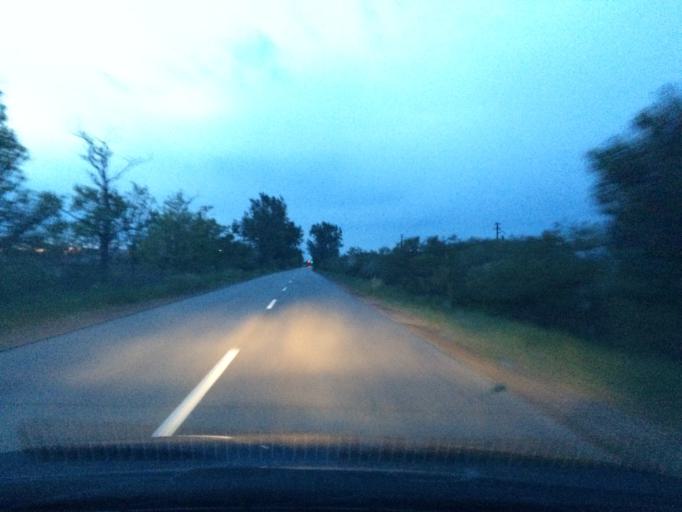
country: HU
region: Szabolcs-Szatmar-Bereg
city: Tiszavasvari
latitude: 47.9252
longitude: 21.3891
